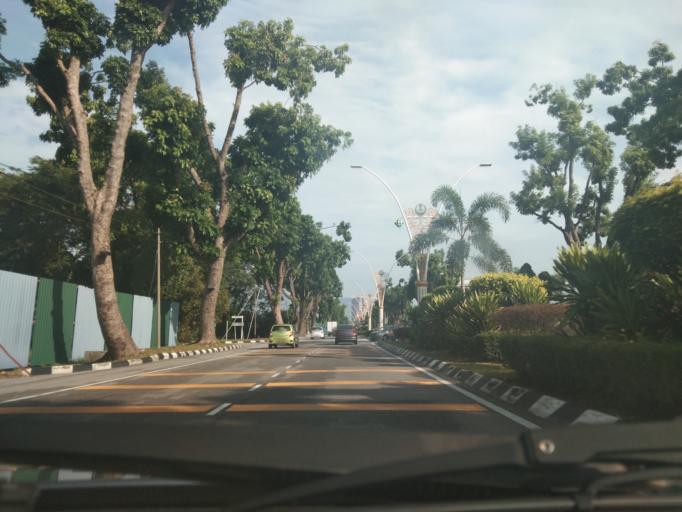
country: MY
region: Perak
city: Ipoh
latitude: 4.5891
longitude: 101.0947
